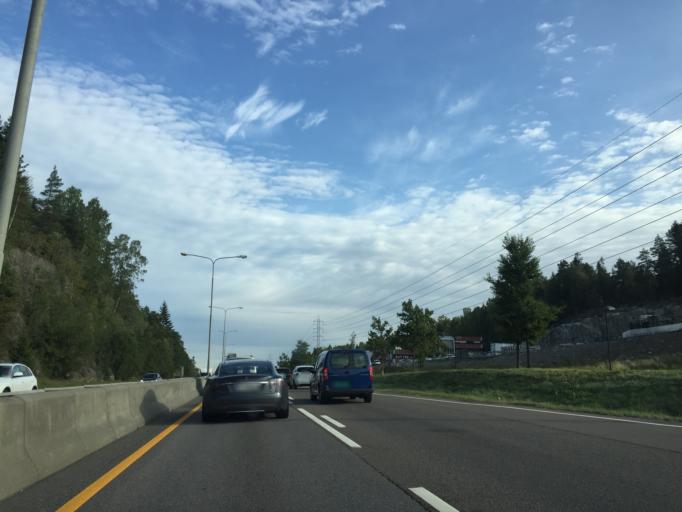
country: NO
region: Akershus
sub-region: Oppegard
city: Kolbotn
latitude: 59.8665
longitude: 10.8303
